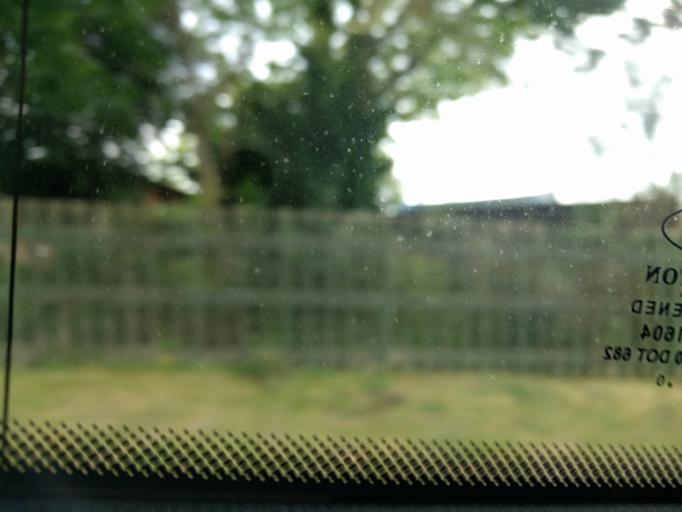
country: GB
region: England
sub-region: Hampshire
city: Brockenhurst
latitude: 50.8196
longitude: -1.5758
